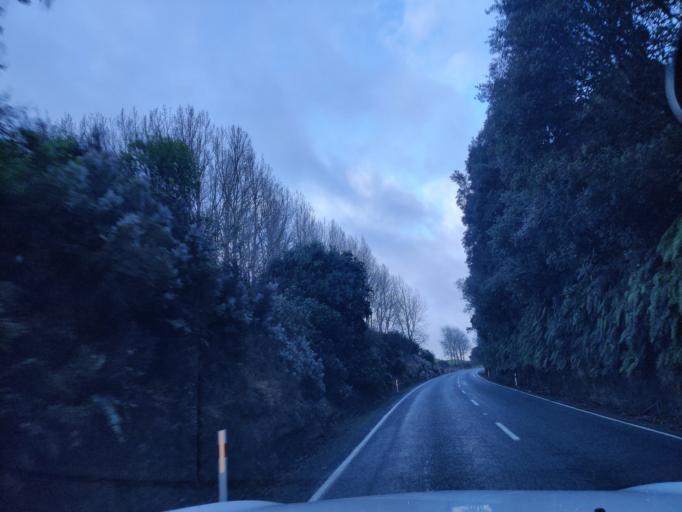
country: NZ
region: Waikato
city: Turangi
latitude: -38.7154
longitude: 175.6613
